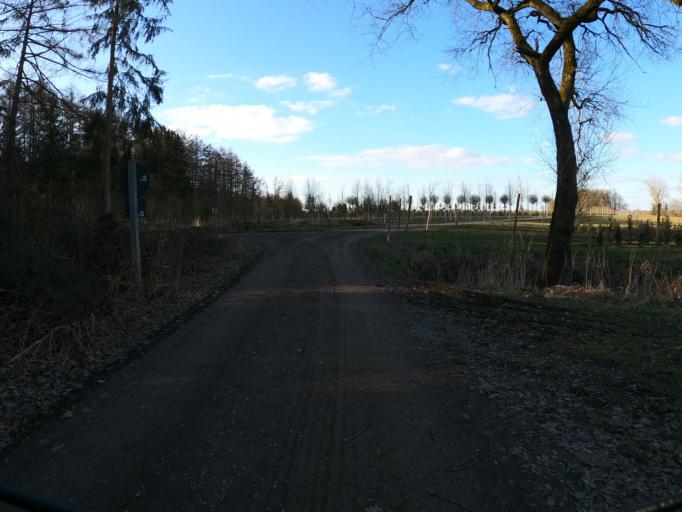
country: DE
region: Bavaria
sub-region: Swabia
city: Leipheim
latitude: 48.4229
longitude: 10.2224
